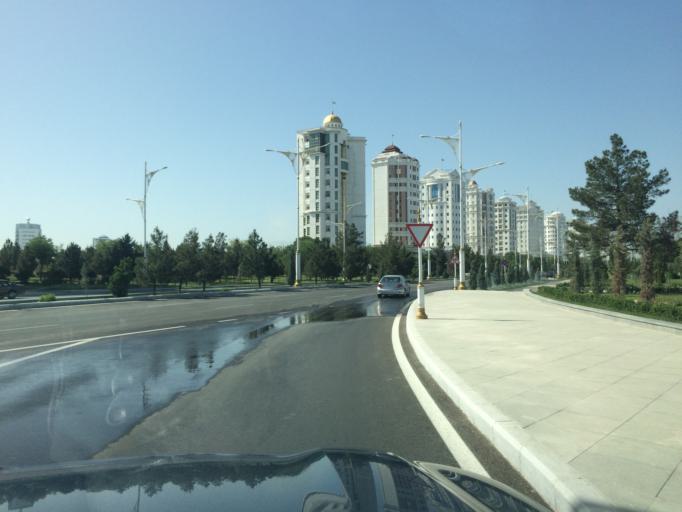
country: TM
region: Ahal
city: Ashgabat
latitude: 37.9249
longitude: 58.3758
